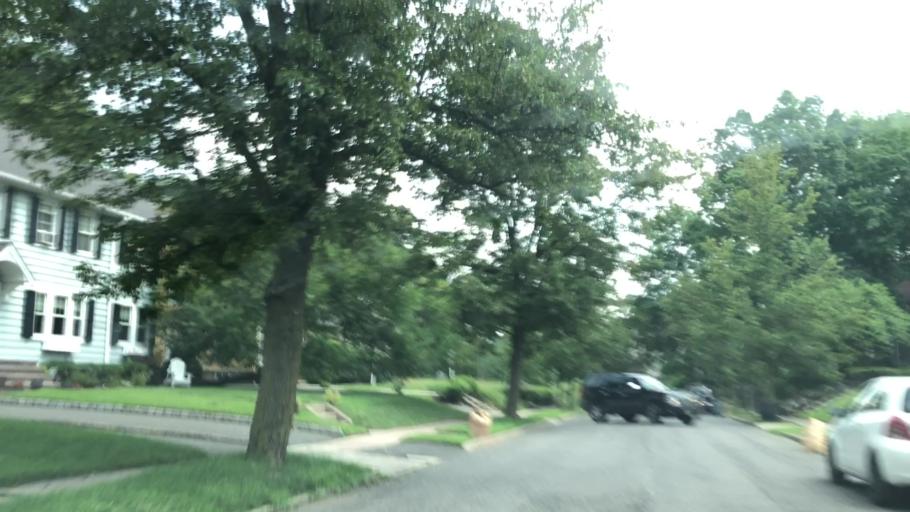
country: US
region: New Jersey
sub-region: Essex County
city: Montclair
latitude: 40.8217
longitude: -74.2004
